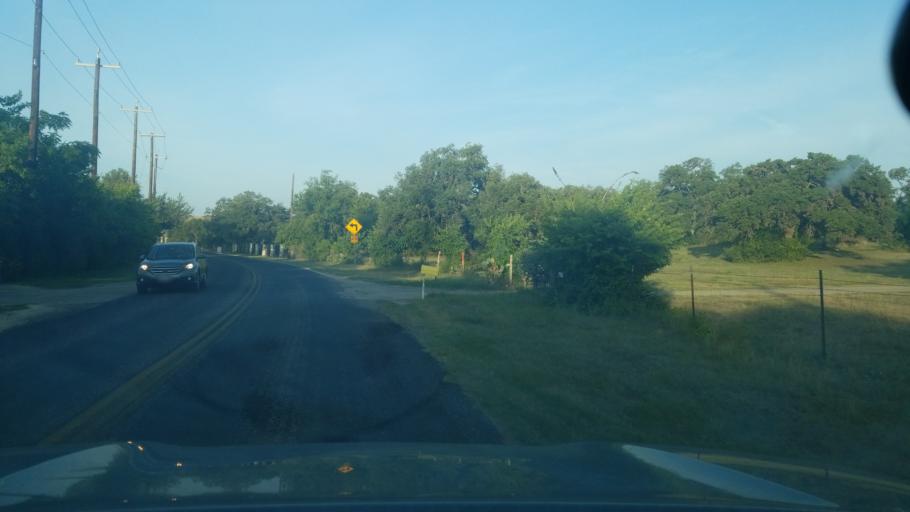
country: US
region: Texas
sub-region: Comal County
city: Bulverde
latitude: 29.7290
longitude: -98.4521
